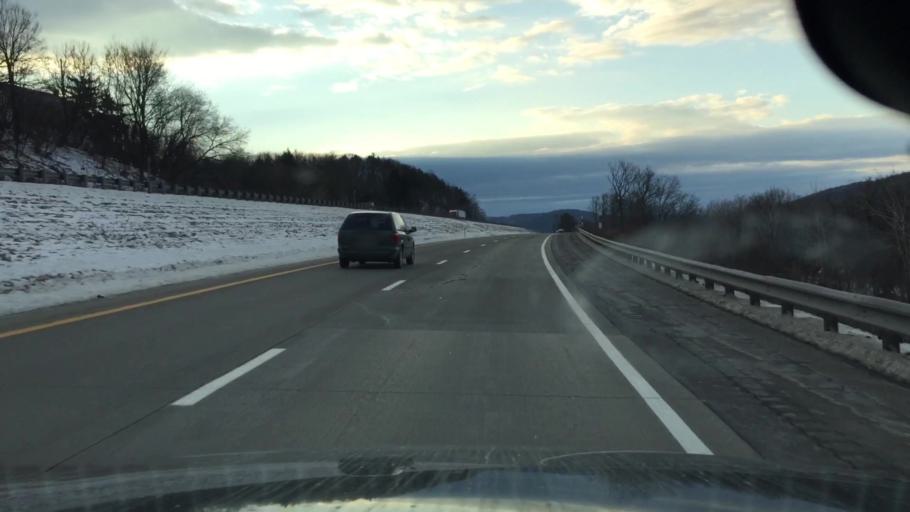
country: US
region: New York
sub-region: Chemung County
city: Elmira
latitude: 42.0552
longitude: -76.7540
